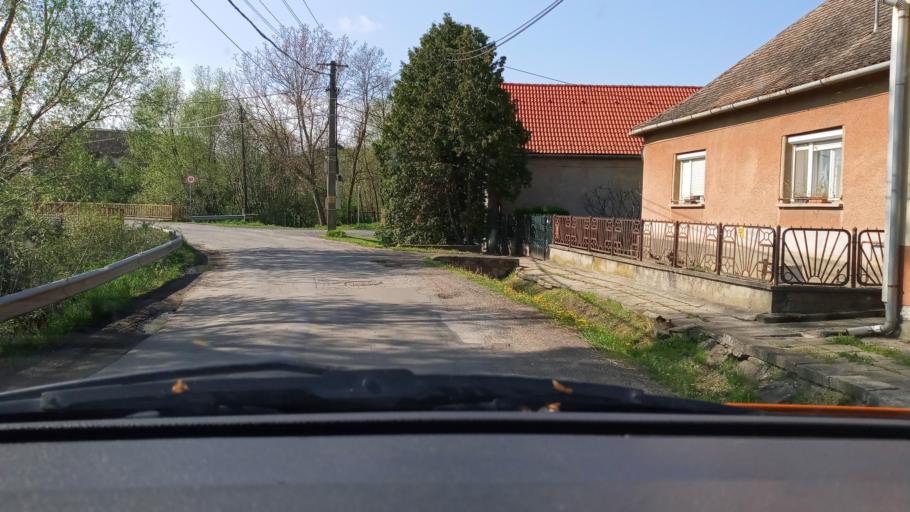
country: HU
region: Baranya
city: Hosszuheteny
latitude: 46.1093
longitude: 18.3419
